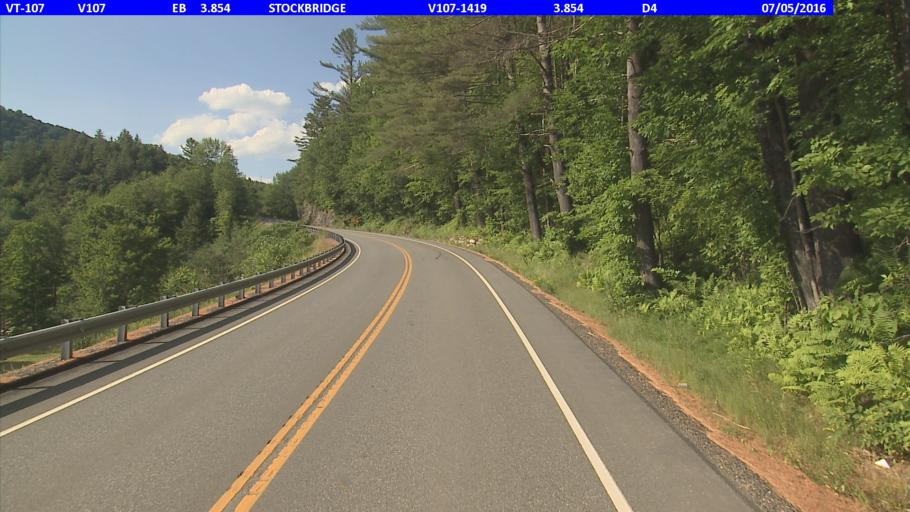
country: US
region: Vermont
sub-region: Orange County
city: Randolph
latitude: 43.7722
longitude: -72.7037
